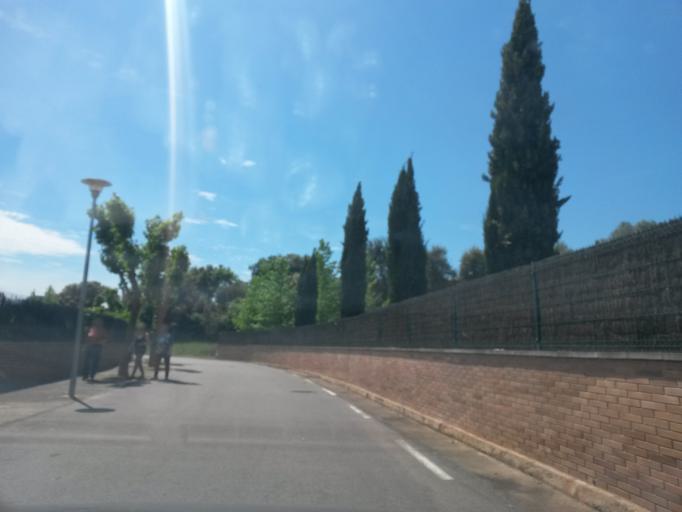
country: ES
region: Catalonia
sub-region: Provincia de Girona
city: Vilablareix
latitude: 41.9613
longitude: 2.7621
